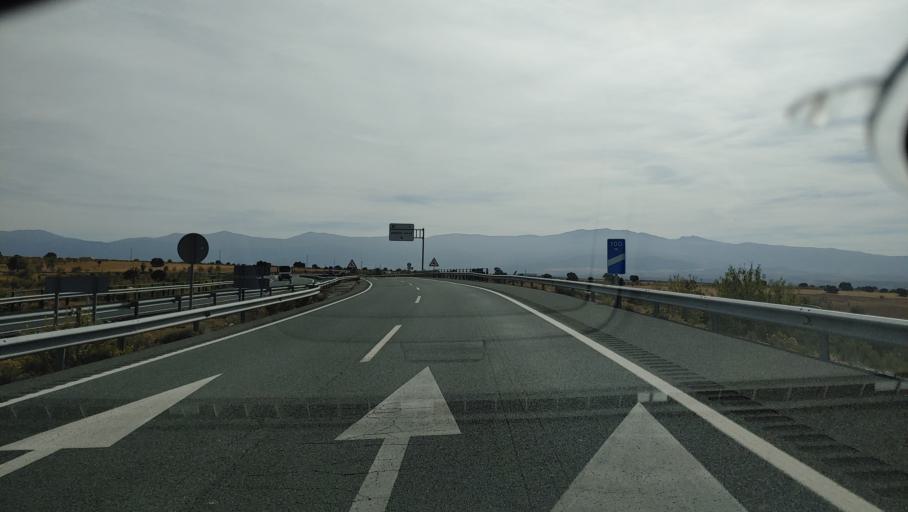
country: ES
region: Andalusia
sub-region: Provincia de Granada
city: Benalua de Guadix
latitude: 37.3728
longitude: -3.0713
